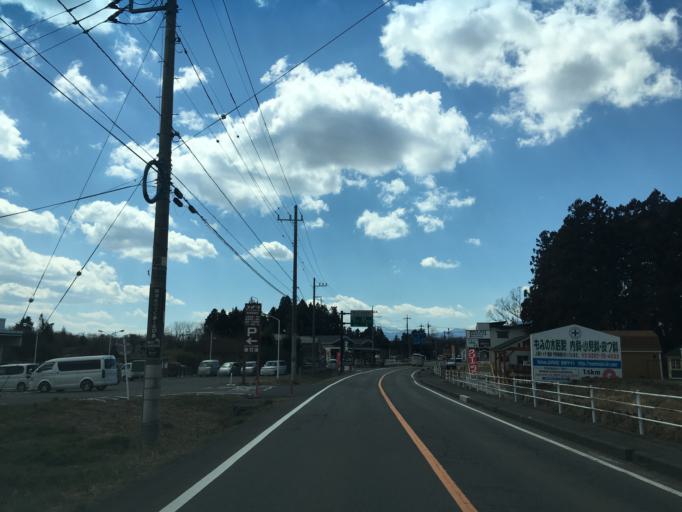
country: JP
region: Tochigi
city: Kuroiso
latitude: 37.0440
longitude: 140.0164
